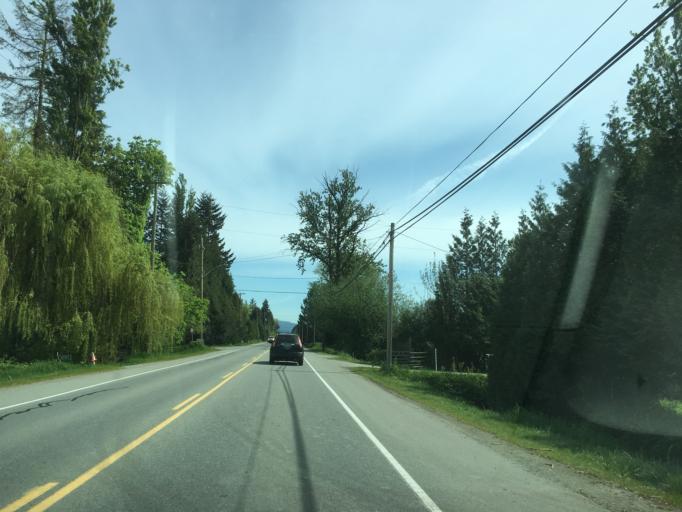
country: CA
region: British Columbia
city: Pitt Meadows
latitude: 49.2442
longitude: -122.7016
